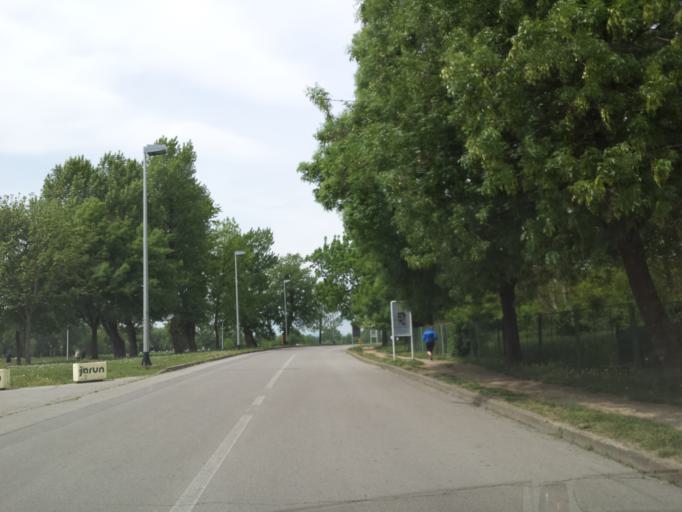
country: HR
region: Grad Zagreb
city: Jankomir
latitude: 45.7804
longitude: 15.9296
